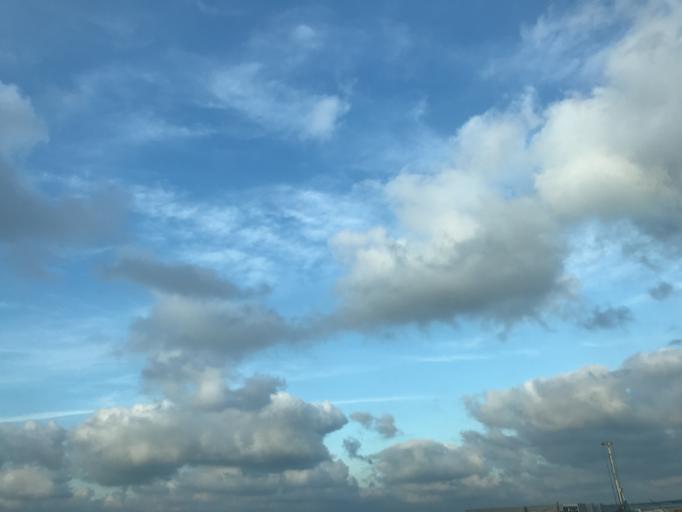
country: TR
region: Istanbul
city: Durusu
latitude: 41.2546
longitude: 28.7090
